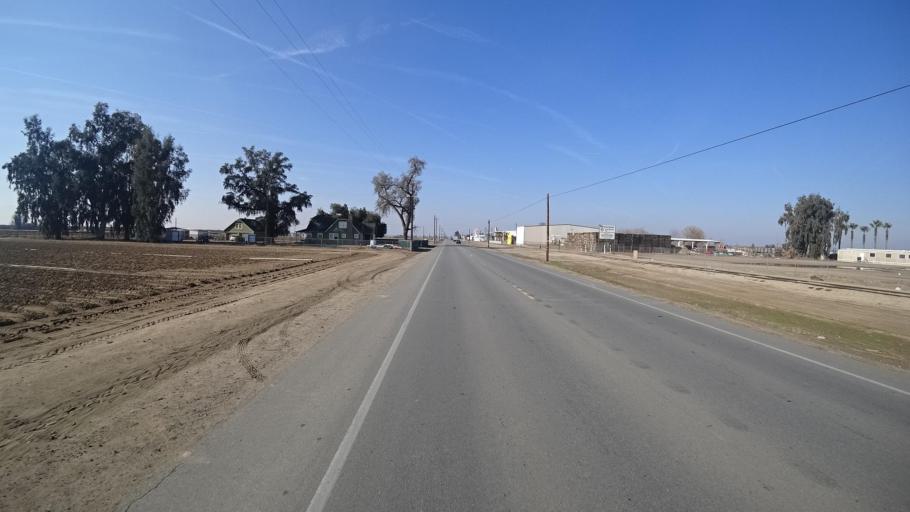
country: US
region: California
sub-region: Kern County
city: Lamont
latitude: 35.2525
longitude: -118.8929
